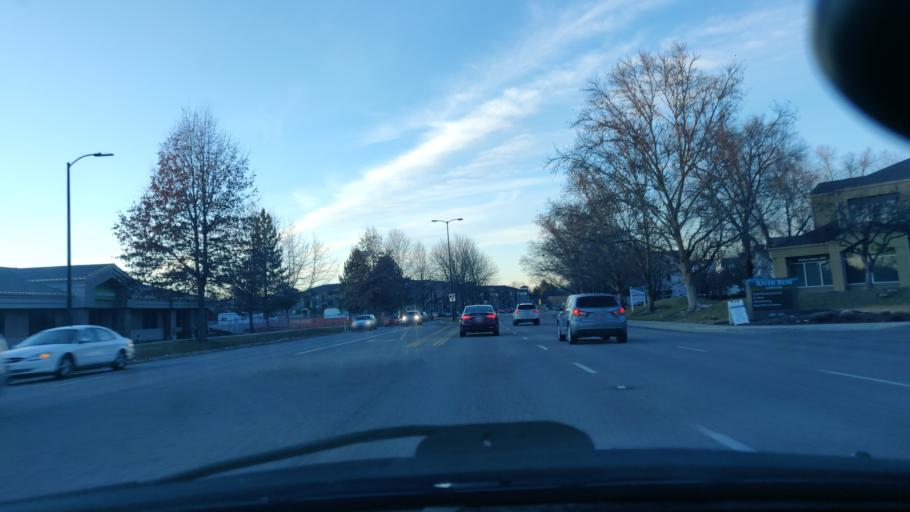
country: US
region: Idaho
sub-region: Ada County
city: Boise
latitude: 43.5906
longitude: -116.1759
